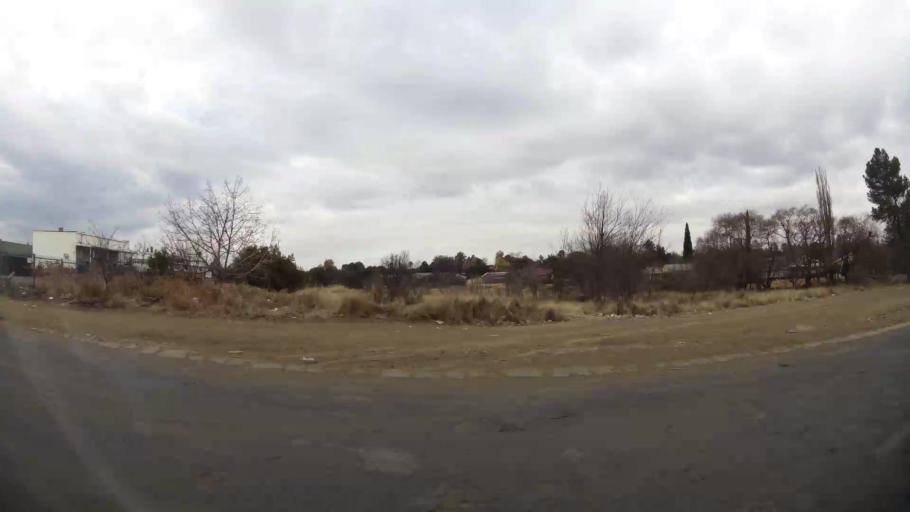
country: ZA
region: Orange Free State
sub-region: Fezile Dabi District Municipality
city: Kroonstad
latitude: -27.6768
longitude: 27.2381
